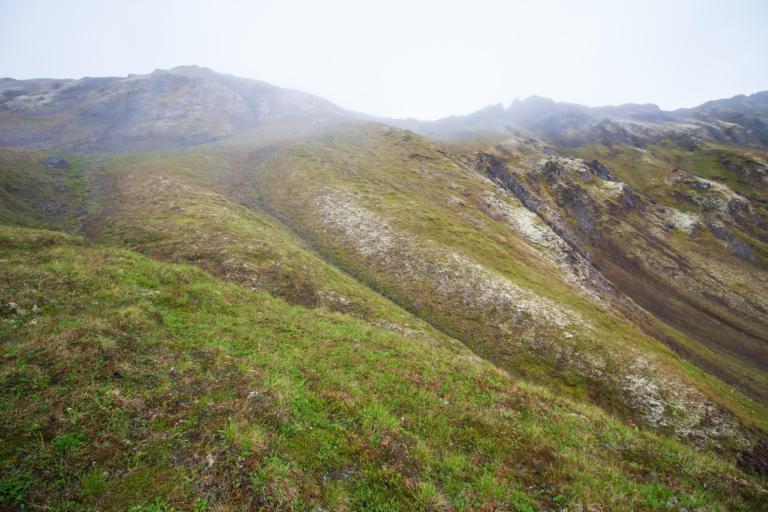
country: RU
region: Kamtsjatka
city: Yelizovo
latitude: 54.0123
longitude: 158.0818
